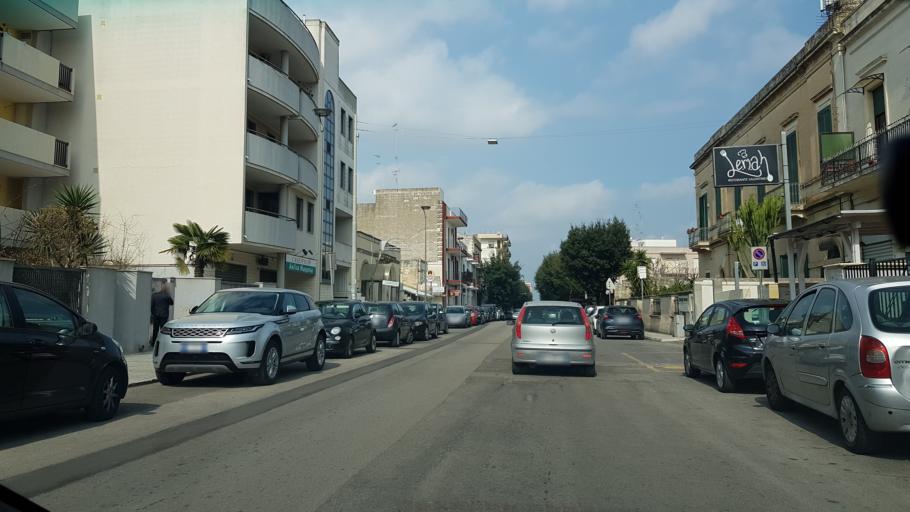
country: IT
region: Apulia
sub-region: Provincia di Lecce
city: Castromediano
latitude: 40.3378
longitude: 18.1776
